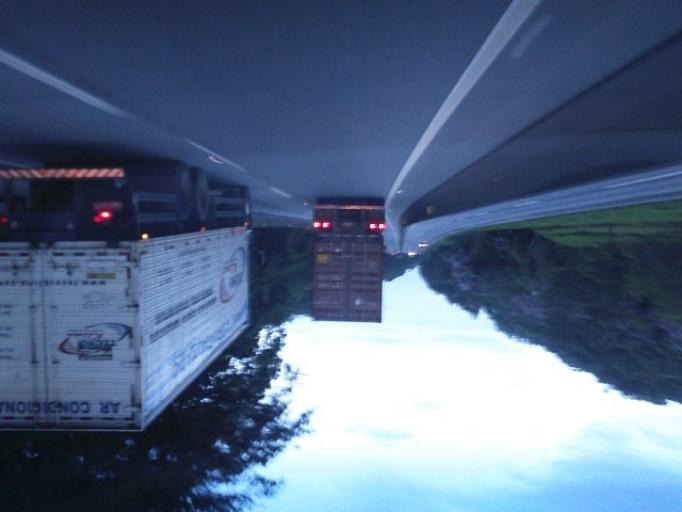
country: BR
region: Santa Catarina
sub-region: Joinville
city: Joinville
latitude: -26.2625
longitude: -48.9022
